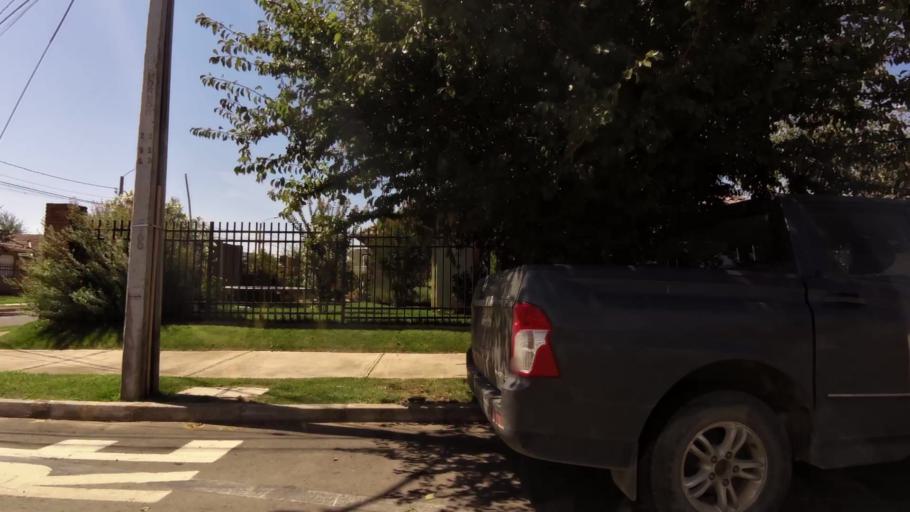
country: CL
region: Maule
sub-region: Provincia de Talca
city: Talca
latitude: -35.4327
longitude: -71.5964
